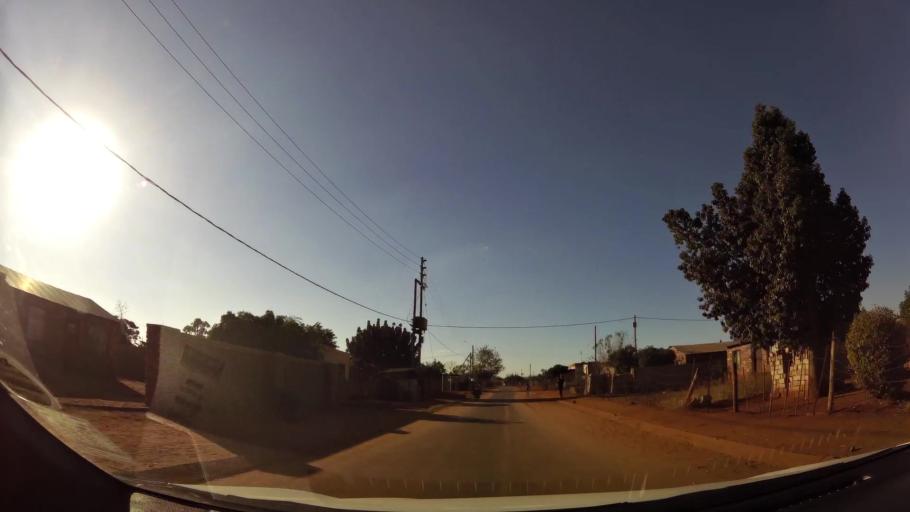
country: ZA
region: Limpopo
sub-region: Waterberg District Municipality
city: Mokopane
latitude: -24.1817
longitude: 28.9775
